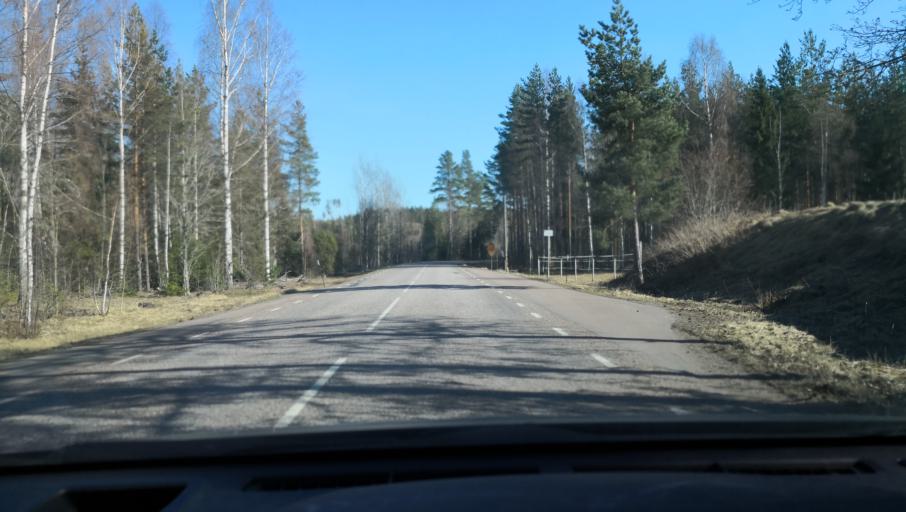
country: SE
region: Dalarna
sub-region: Avesta Kommun
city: Avesta
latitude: 60.0153
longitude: 16.3406
